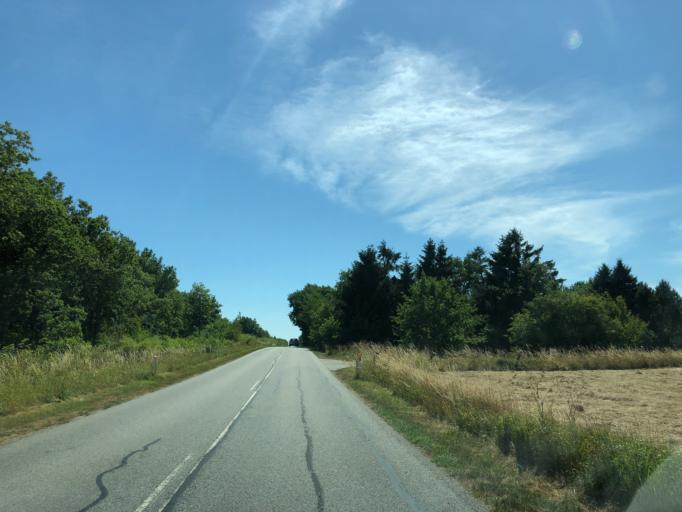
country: DK
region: Central Jutland
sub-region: Skive Kommune
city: Skive
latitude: 56.5220
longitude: 9.0306
